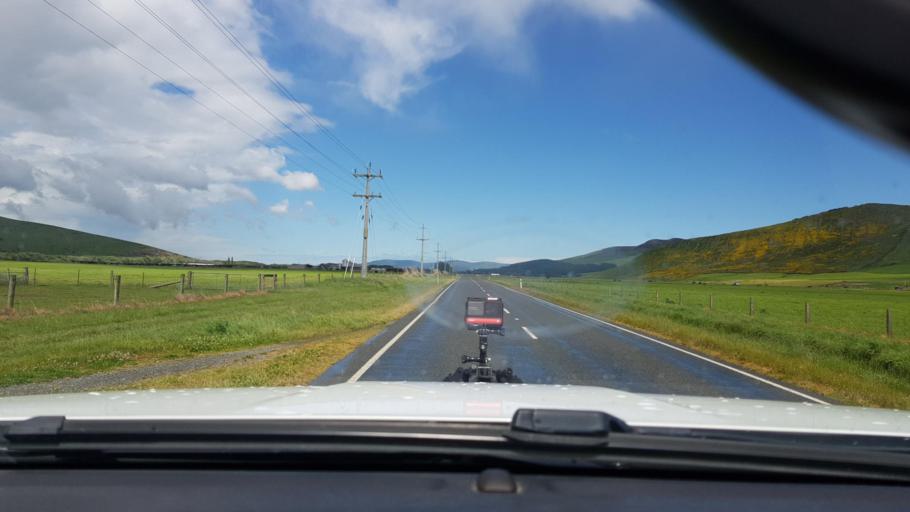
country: NZ
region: Southland
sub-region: Southland District
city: Winton
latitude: -45.7779
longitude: 168.3990
